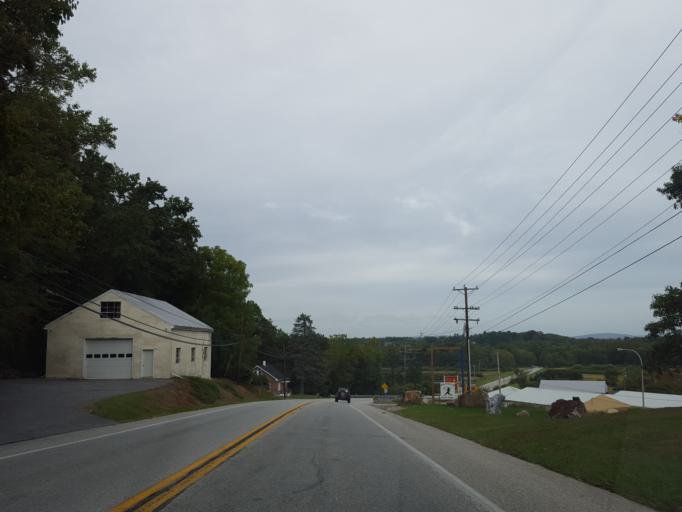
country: US
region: Pennsylvania
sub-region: York County
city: West York
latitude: 39.9140
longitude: -76.7936
